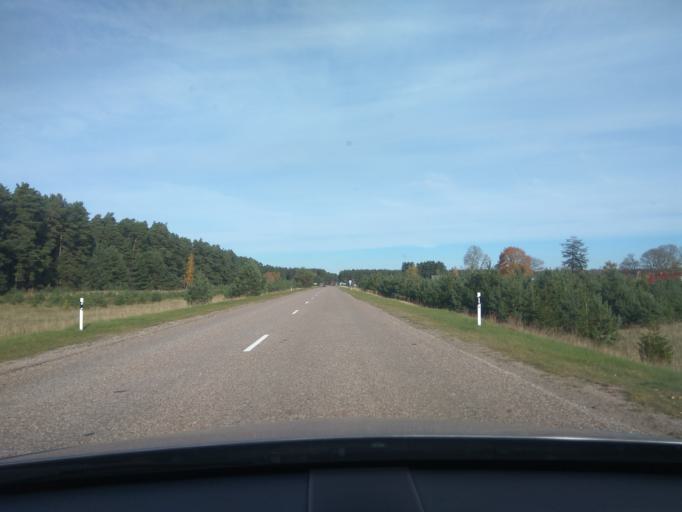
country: LV
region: Alsunga
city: Alsunga
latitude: 57.0081
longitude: 21.3883
